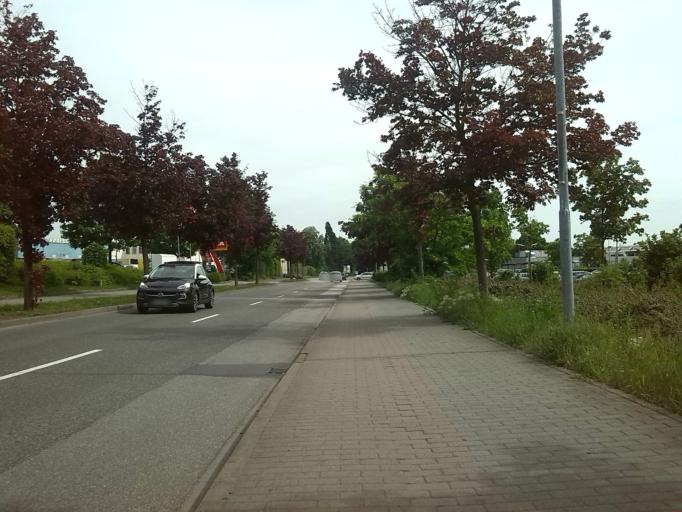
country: DE
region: Baden-Wuerttemberg
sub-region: Karlsruhe Region
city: Ladenburg
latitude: 49.4803
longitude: 8.6034
